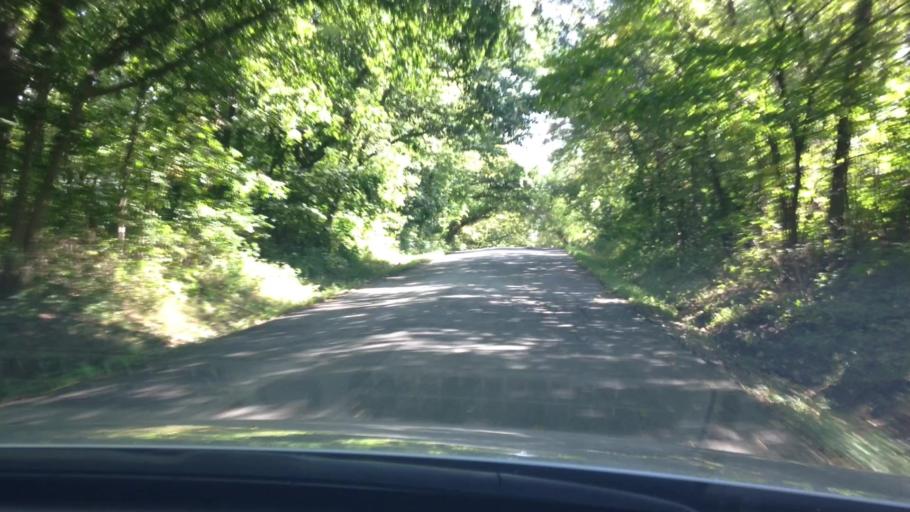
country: US
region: Missouri
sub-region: Platte County
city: Weatherby Lake
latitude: 39.3312
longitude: -94.6676
